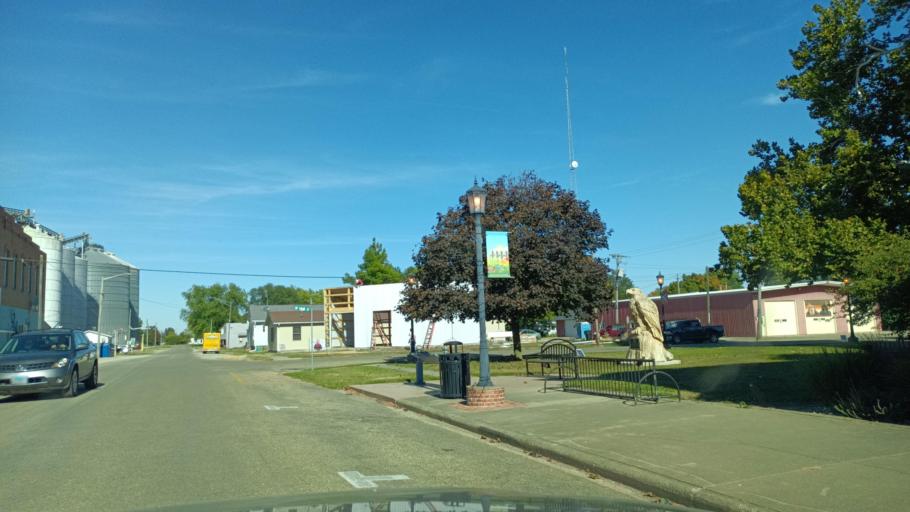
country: US
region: Illinois
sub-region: Logan County
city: Atlanta
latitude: 40.2607
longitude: -89.2314
